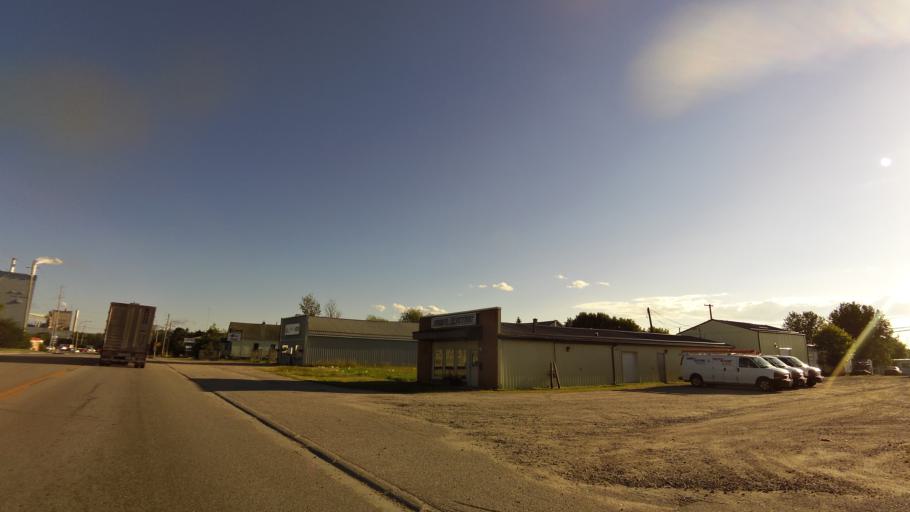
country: CA
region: Ontario
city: Dryden
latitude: 49.7901
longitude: -92.8474
